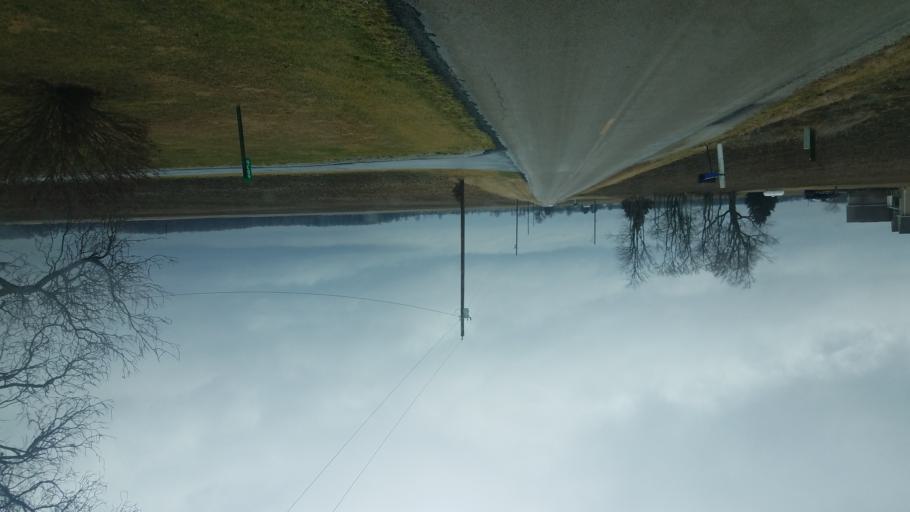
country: US
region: Ohio
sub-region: Hardin County
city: Forest
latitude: 40.7186
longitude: -83.5145
